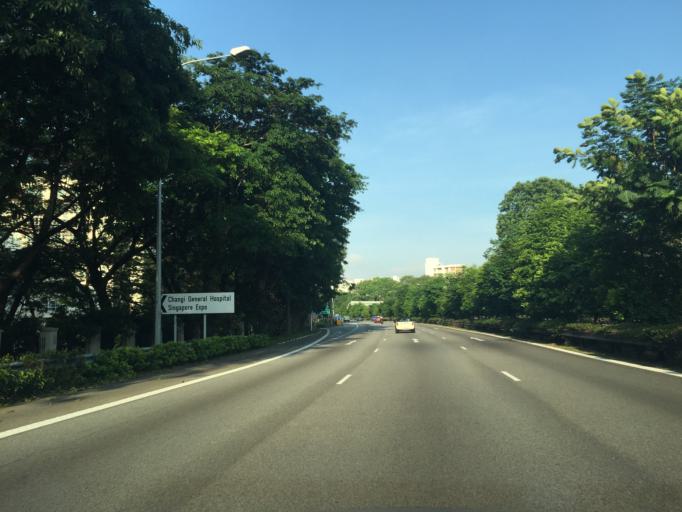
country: SG
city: Singapore
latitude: 1.3503
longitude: 103.9585
